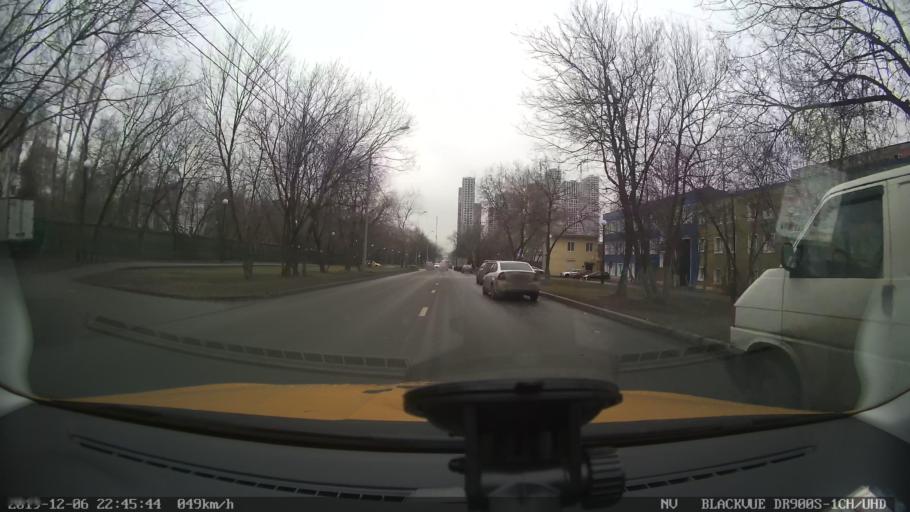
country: RU
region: Moscow
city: Metrogorodok
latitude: 55.8100
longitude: 37.7689
